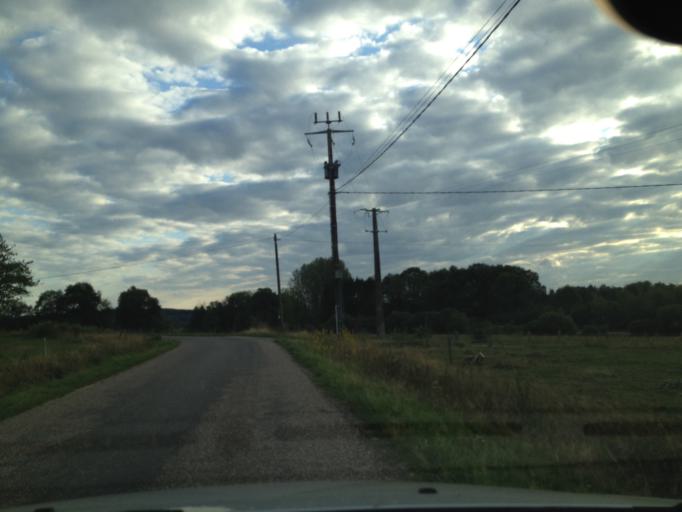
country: FR
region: Lorraine
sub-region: Departement des Vosges
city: Bains-les-Bains
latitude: 47.9932
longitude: 6.2093
